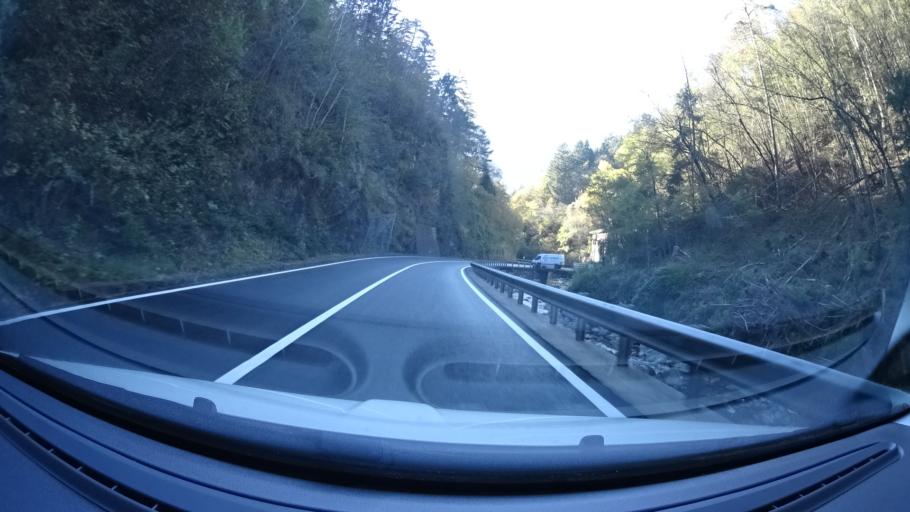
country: IT
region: Trentino-Alto Adige
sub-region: Bolzano
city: Ponte Gardena
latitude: 46.5987
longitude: 11.5441
